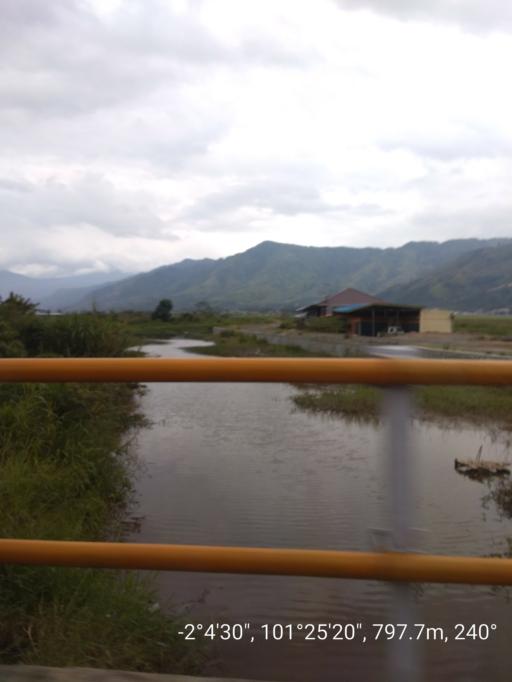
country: ID
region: Jambi
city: Sungai Penuh
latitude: -2.0750
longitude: 101.4224
